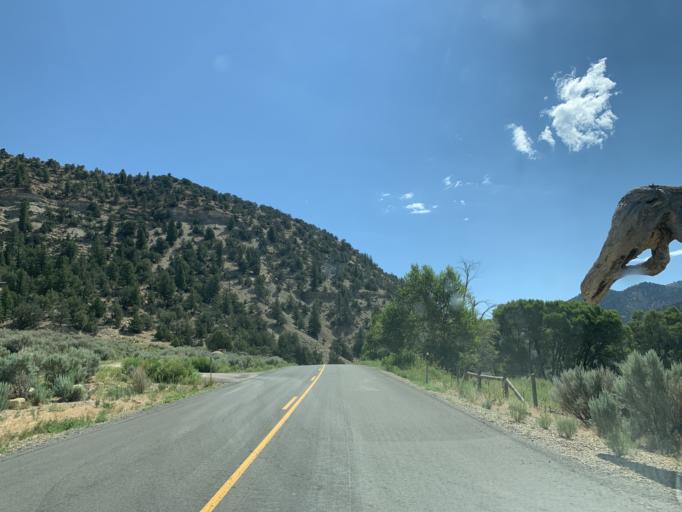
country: US
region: Utah
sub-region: Carbon County
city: East Carbon City
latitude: 39.7765
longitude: -110.4682
